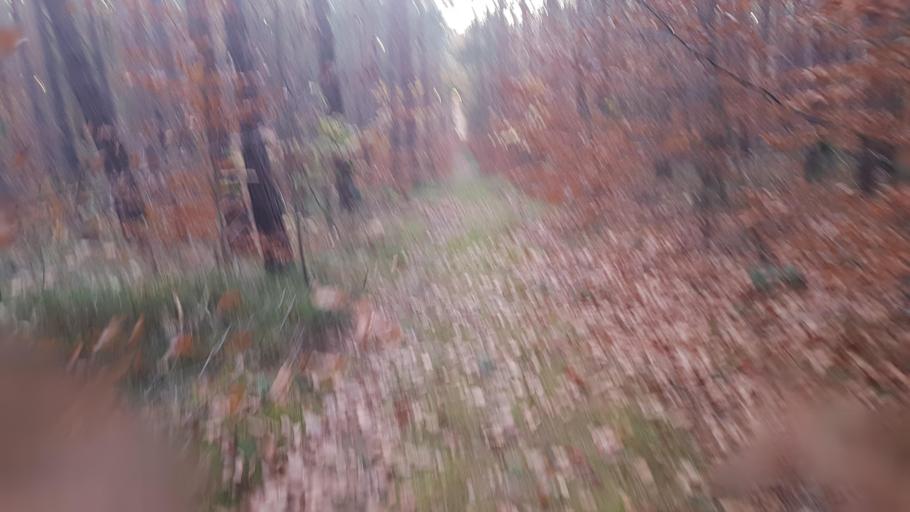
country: DE
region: Brandenburg
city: Merzdorf
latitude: 51.3997
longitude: 13.5419
